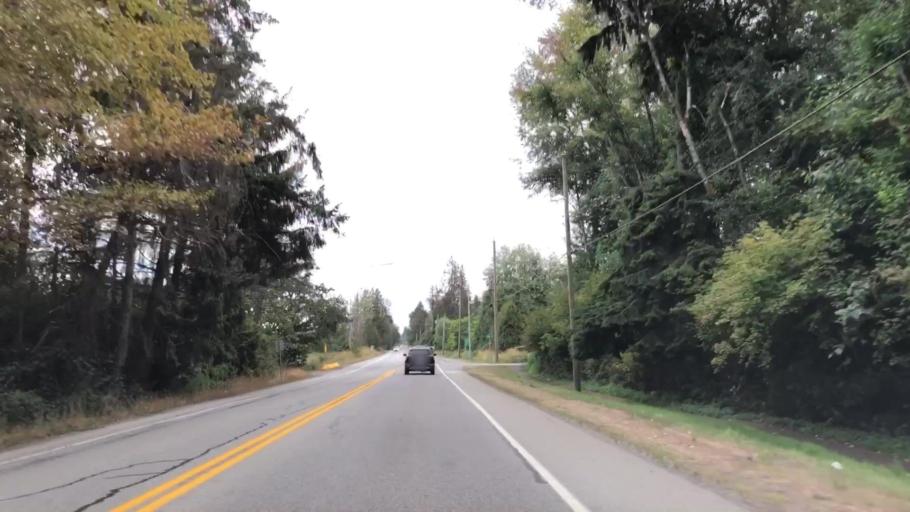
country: US
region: Washington
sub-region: Whatcom County
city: Blaine
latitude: 49.0601
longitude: -122.7470
